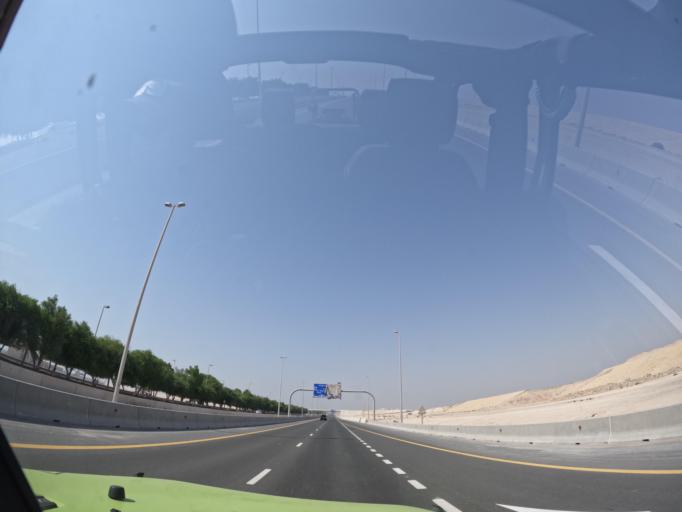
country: AE
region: Abu Dhabi
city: Abu Dhabi
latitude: 24.4251
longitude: 54.6781
